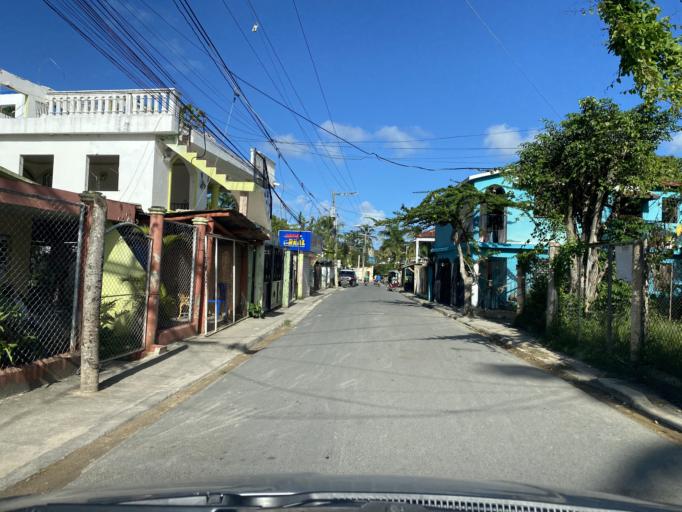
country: DO
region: Samana
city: Las Terrenas
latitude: 19.3129
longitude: -69.5457
